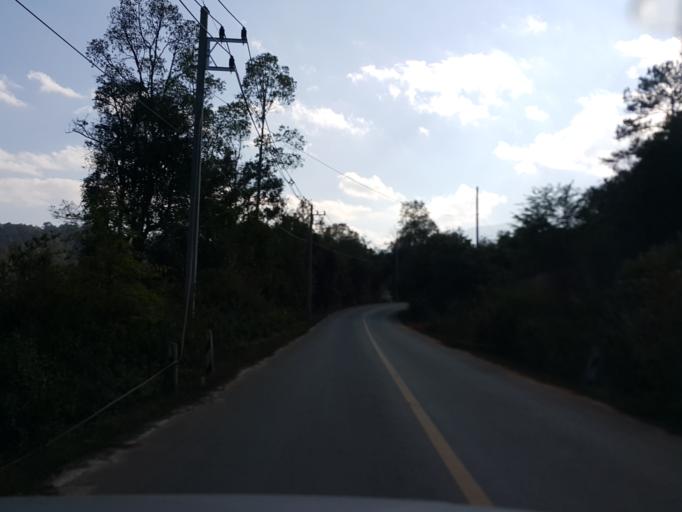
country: TH
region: Chiang Mai
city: Mae Wang
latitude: 18.6620
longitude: 98.5492
